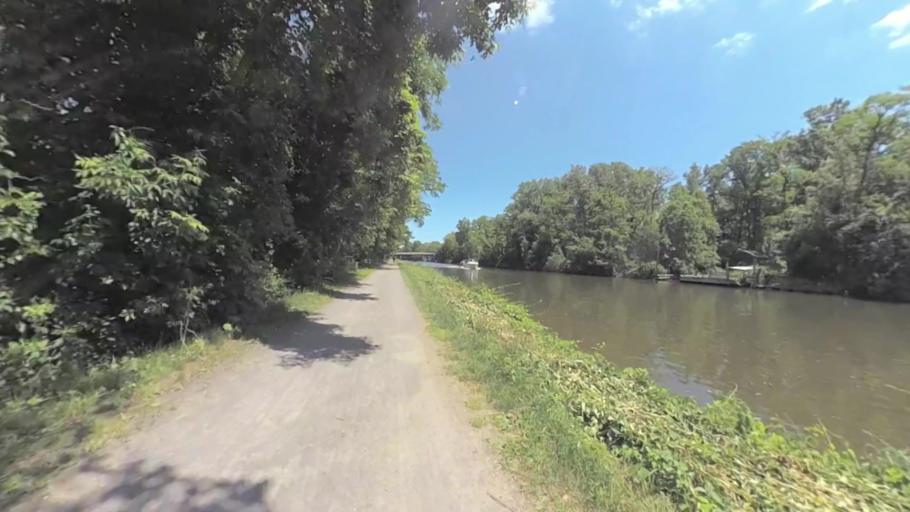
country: US
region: New York
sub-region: Monroe County
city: Fairport
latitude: 43.0771
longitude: -77.4625
